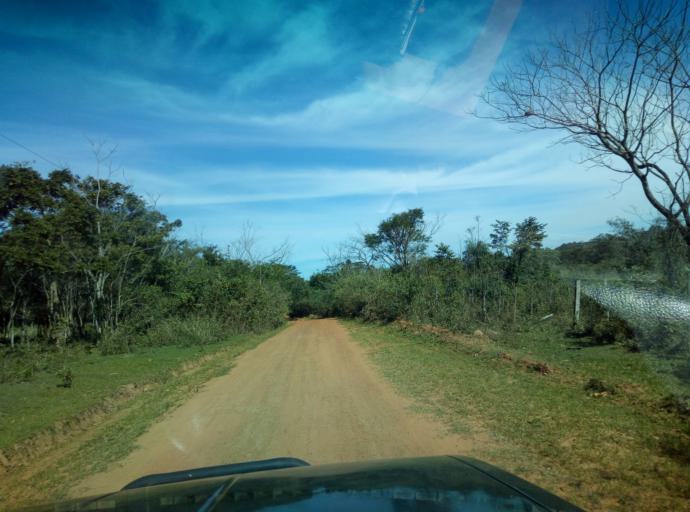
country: PY
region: Caaguazu
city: Carayao
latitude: -25.1870
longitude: -56.2548
